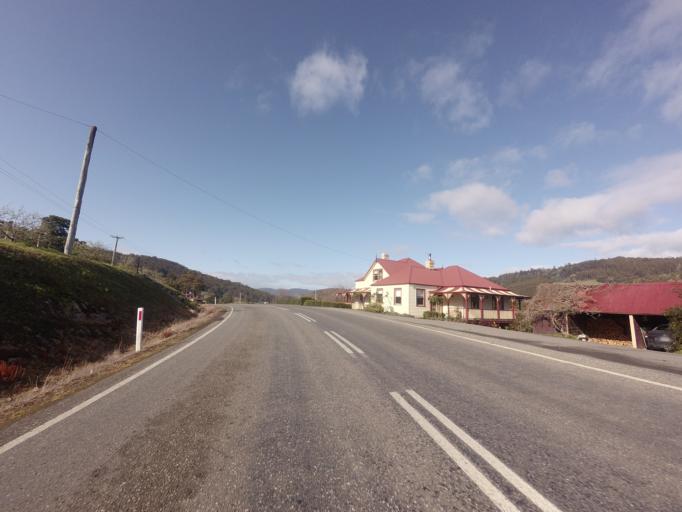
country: AU
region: Tasmania
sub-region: Huon Valley
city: Cygnet
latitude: -43.2842
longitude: 147.0108
